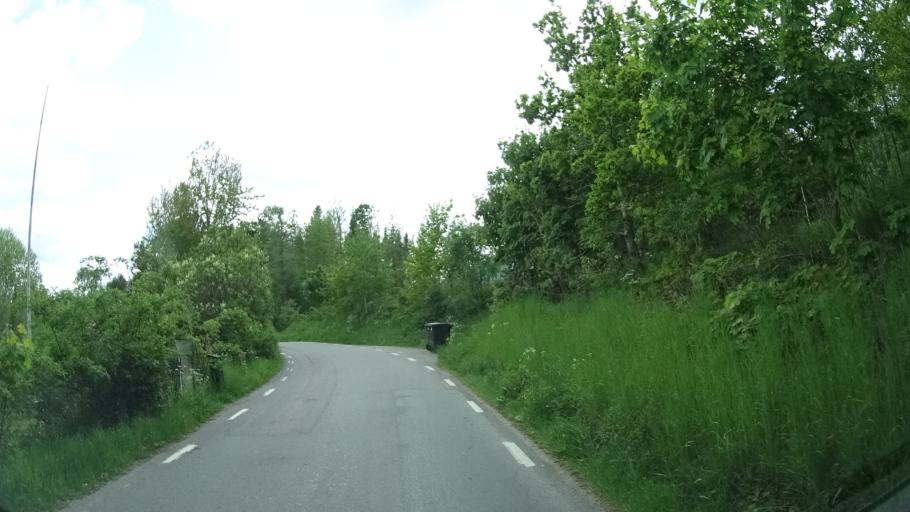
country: SE
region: OEstergoetland
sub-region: Finspangs Kommun
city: Finspang
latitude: 58.5908
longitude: 15.7745
